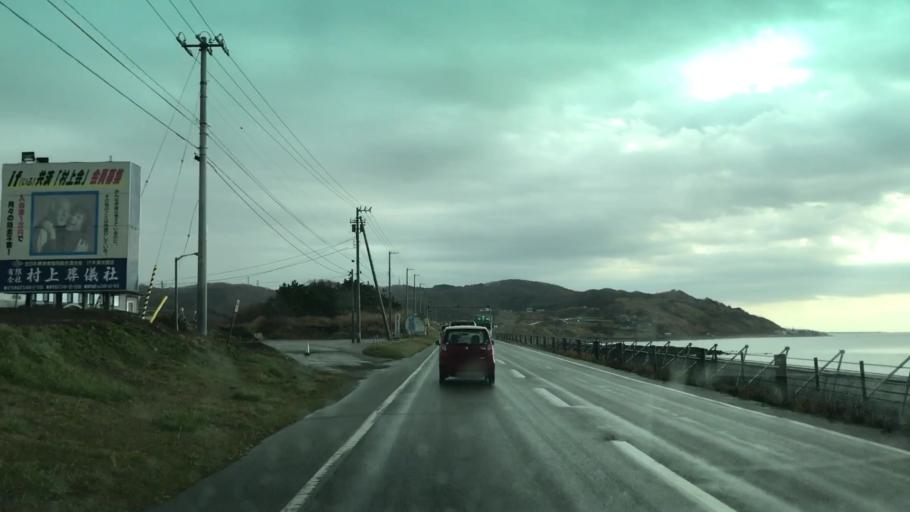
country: JP
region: Hokkaido
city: Shizunai-furukawacho
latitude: 42.1866
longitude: 142.7134
